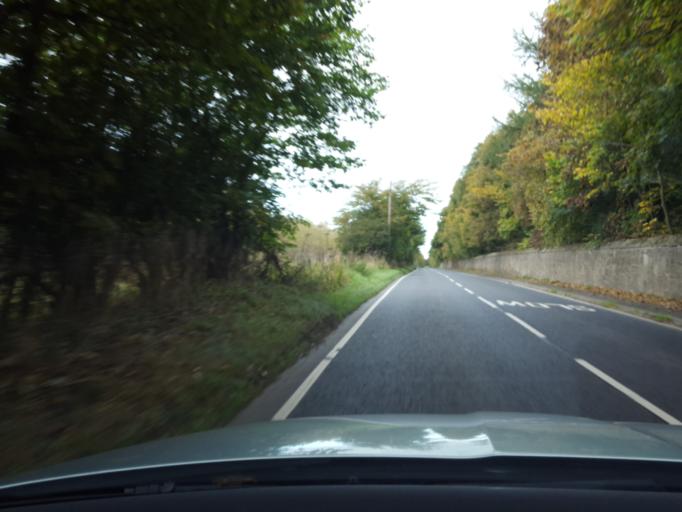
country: GB
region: Scotland
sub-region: Fife
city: Pathhead
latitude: 55.8606
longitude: -2.9995
